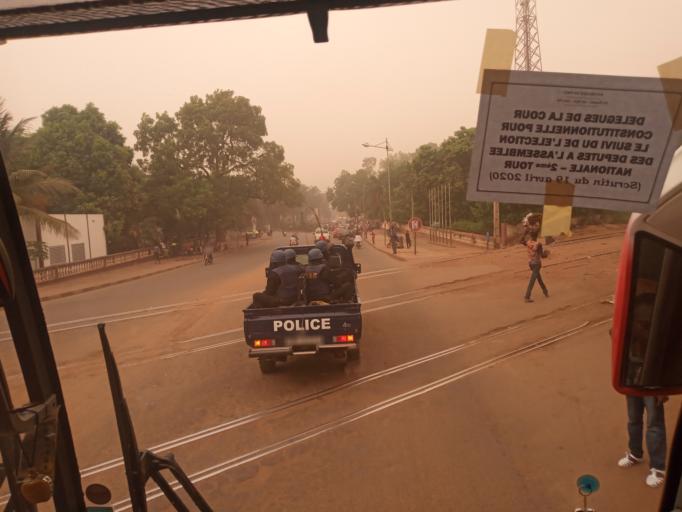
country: ML
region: Bamako
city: Bamako
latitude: 12.6490
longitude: -7.9993
